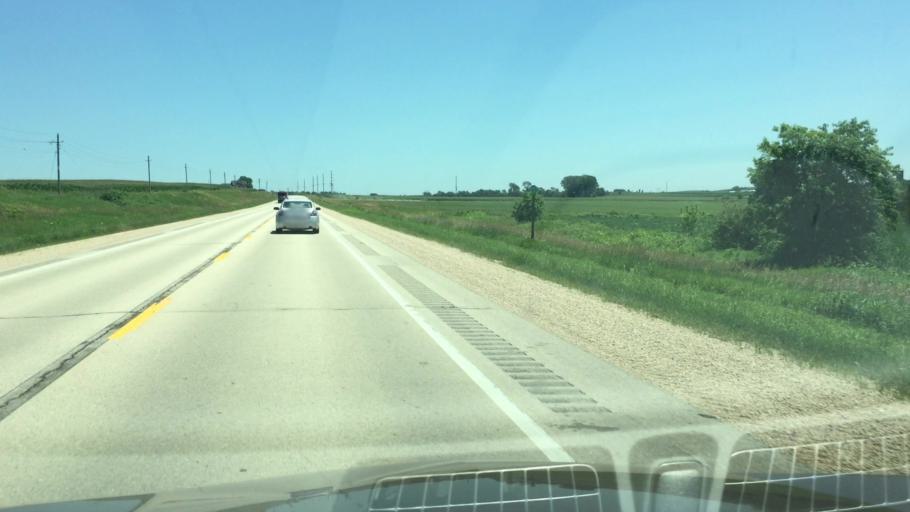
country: US
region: Iowa
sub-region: Jackson County
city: Maquoketa
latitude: 42.0687
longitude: -90.7884
